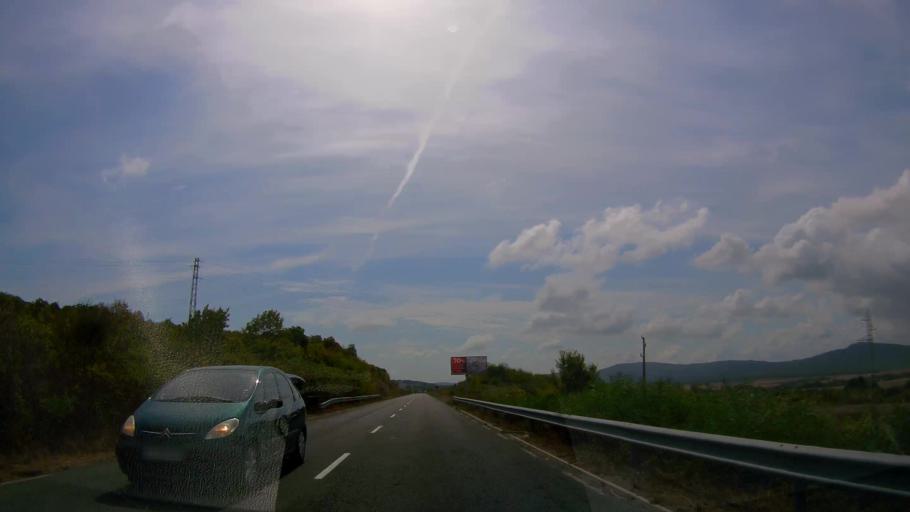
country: BG
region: Burgas
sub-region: Obshtina Sozopol
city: Sozopol
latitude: 42.3902
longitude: 27.6776
